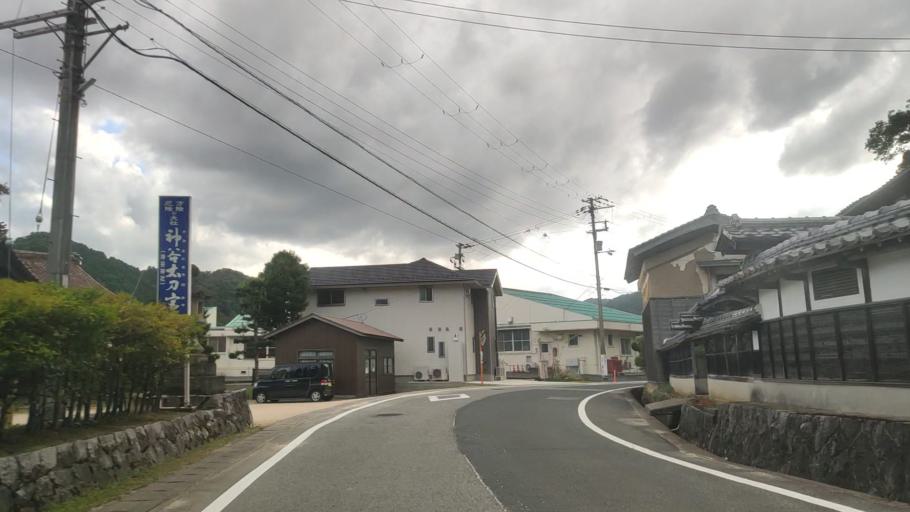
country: JP
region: Hyogo
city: Toyooka
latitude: 35.6040
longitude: 134.8923
